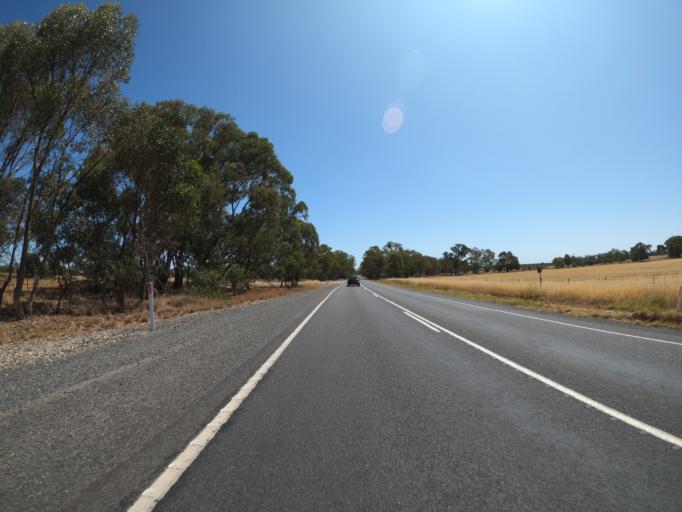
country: AU
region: New South Wales
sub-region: Corowa Shire
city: Corowa
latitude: -36.0573
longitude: 146.4386
